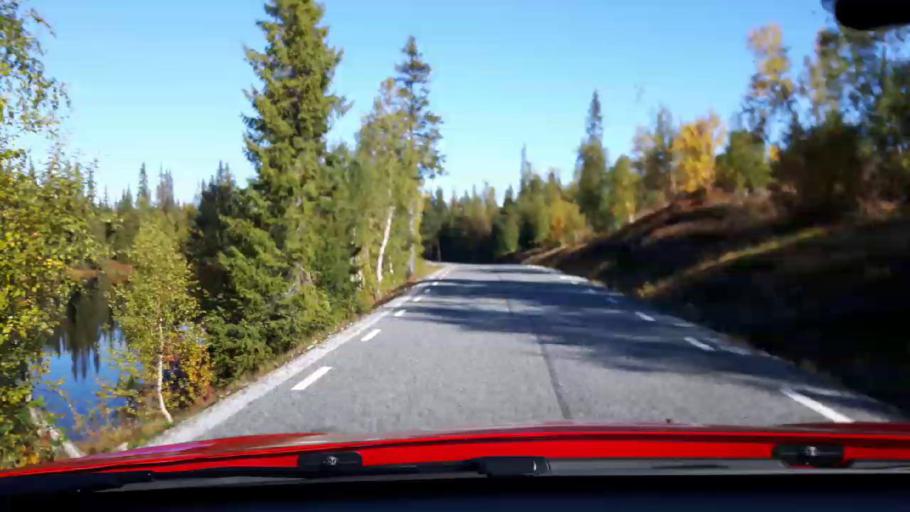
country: NO
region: Nord-Trondelag
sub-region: Lierne
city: Sandvika
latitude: 64.6135
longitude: 13.7016
